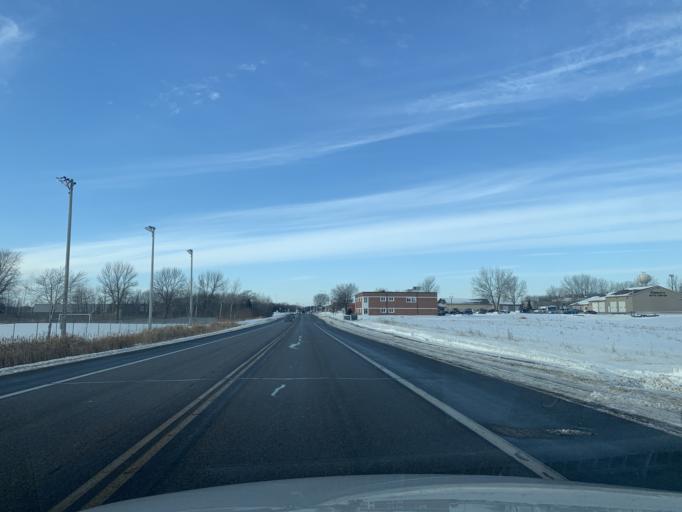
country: US
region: Minnesota
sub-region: Wright County
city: Buffalo
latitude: 45.1656
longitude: -93.8506
